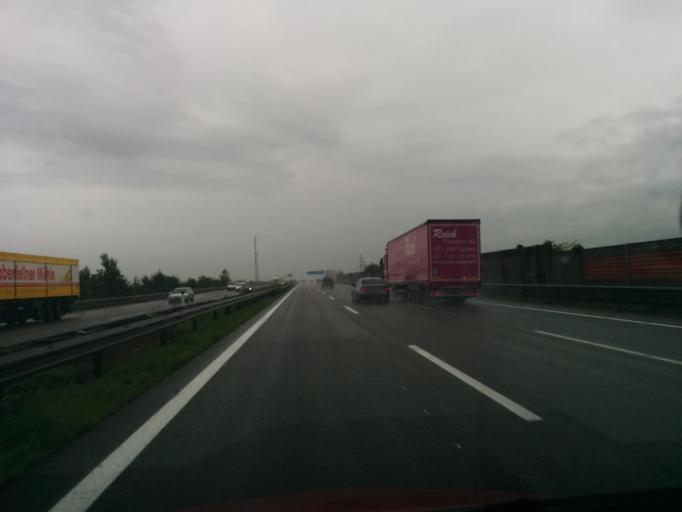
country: AT
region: Lower Austria
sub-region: Politischer Bezirk Sankt Polten
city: Gerersdorf
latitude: 48.1777
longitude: 15.5839
